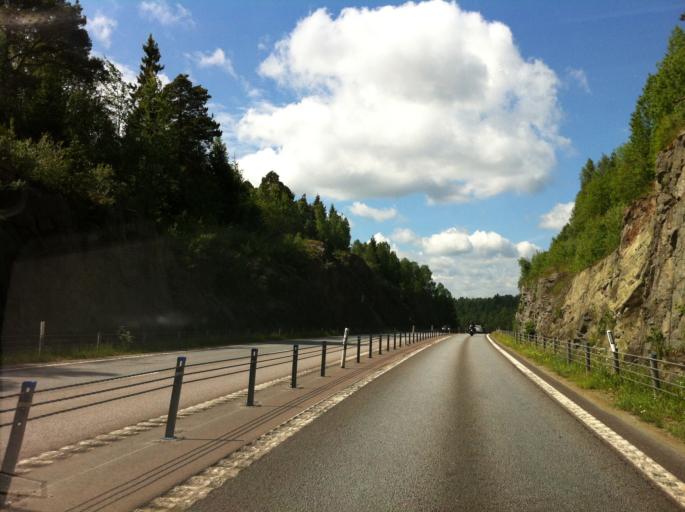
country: SE
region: Vaermland
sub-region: Grums Kommun
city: Grums
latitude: 59.3482
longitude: 13.1218
